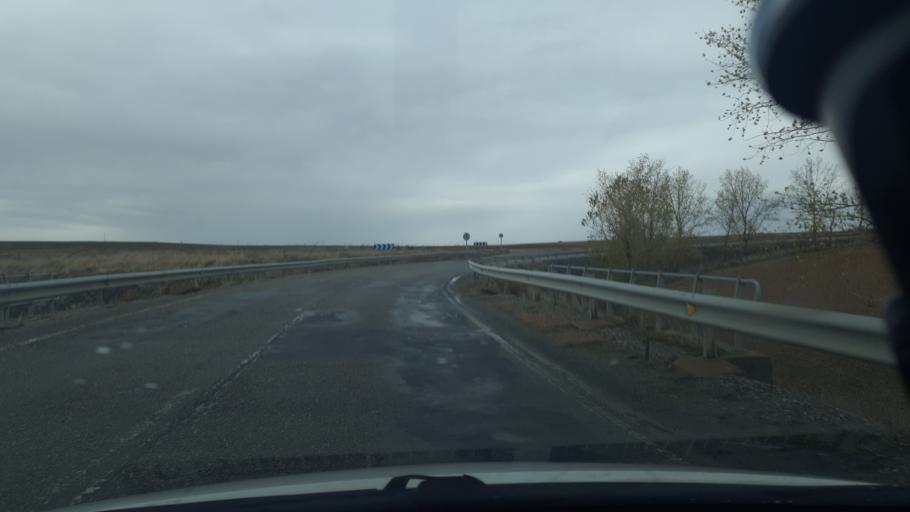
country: ES
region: Castille and Leon
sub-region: Provincia de Segovia
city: Segovia
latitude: 40.9664
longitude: -4.1405
